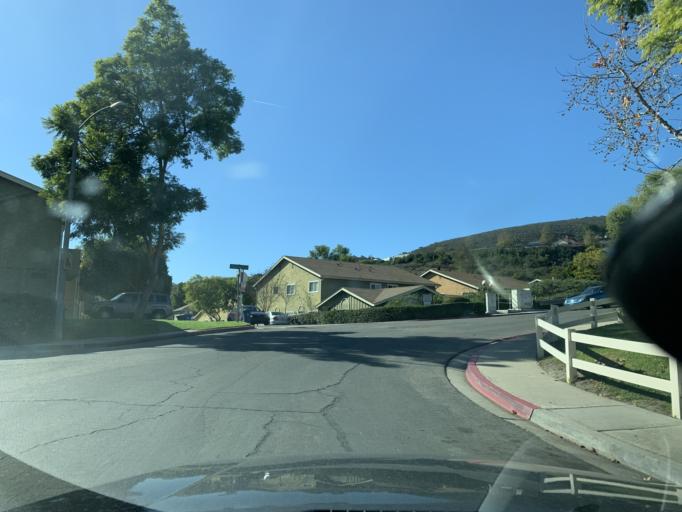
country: US
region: California
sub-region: San Diego County
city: Poway
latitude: 32.9659
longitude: -117.0987
